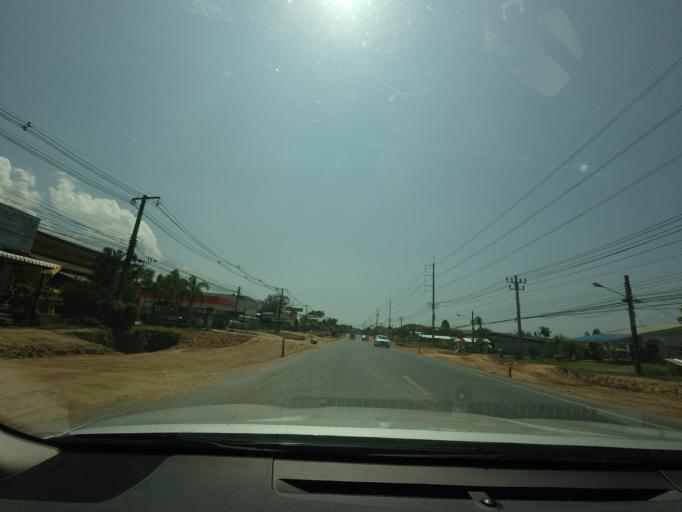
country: TH
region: Phangnga
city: Ban Khao Lak
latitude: 8.6933
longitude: 98.2547
